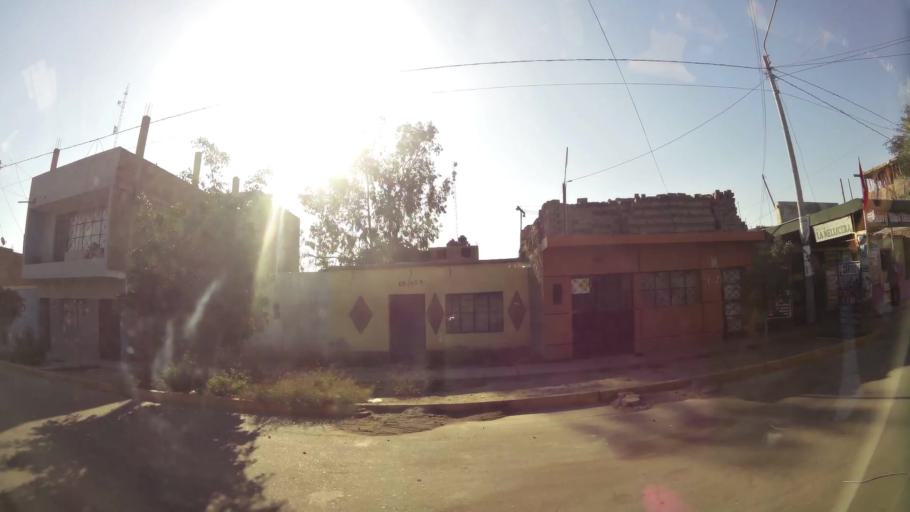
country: PE
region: Ica
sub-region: Provincia de Ica
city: La Tinguina
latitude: -14.0451
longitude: -75.7000
